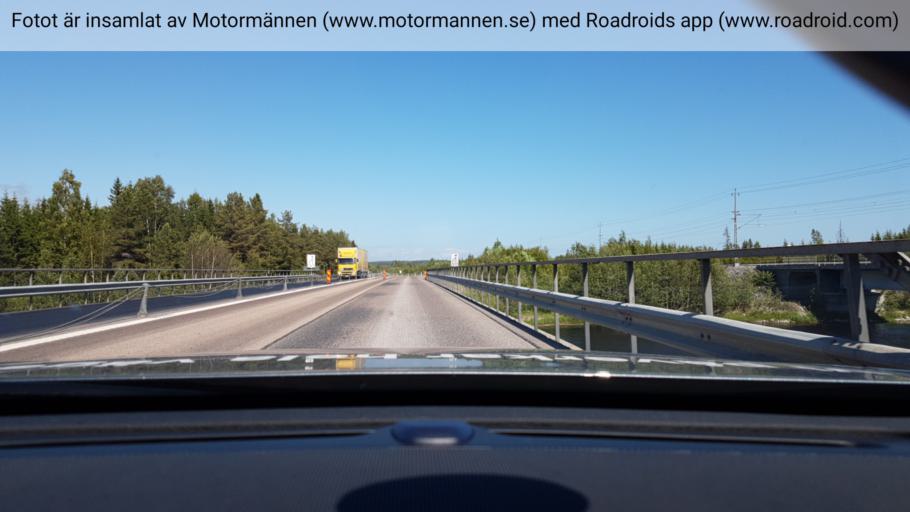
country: SE
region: Vaesterbotten
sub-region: Nordmalings Kommun
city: Nordmaling
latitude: 63.5588
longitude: 19.4245
